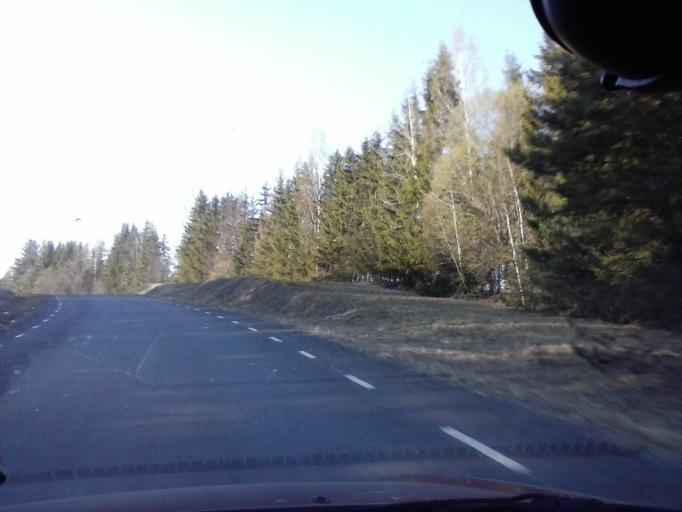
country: EE
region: Tartu
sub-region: UElenurme vald
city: Ulenurme
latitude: 58.1759
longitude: 26.8322
